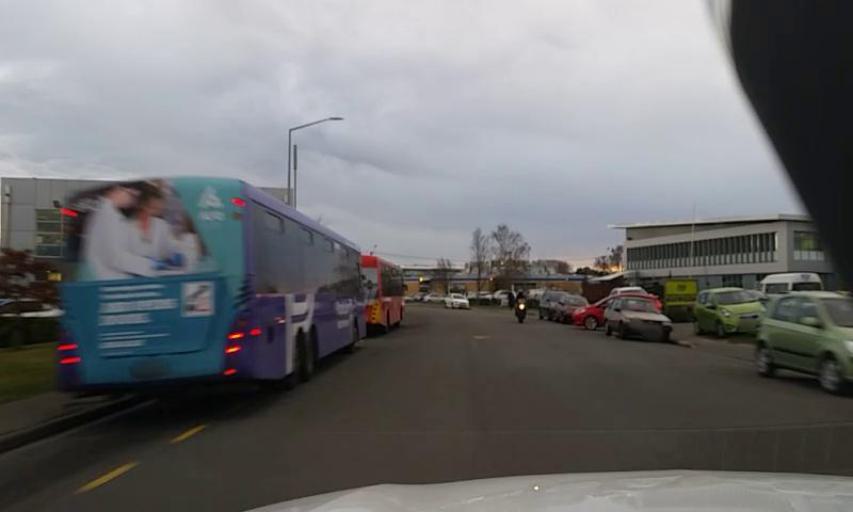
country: NZ
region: Canterbury
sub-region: Christchurch City
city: Christchurch
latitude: -43.4895
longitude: 172.5620
